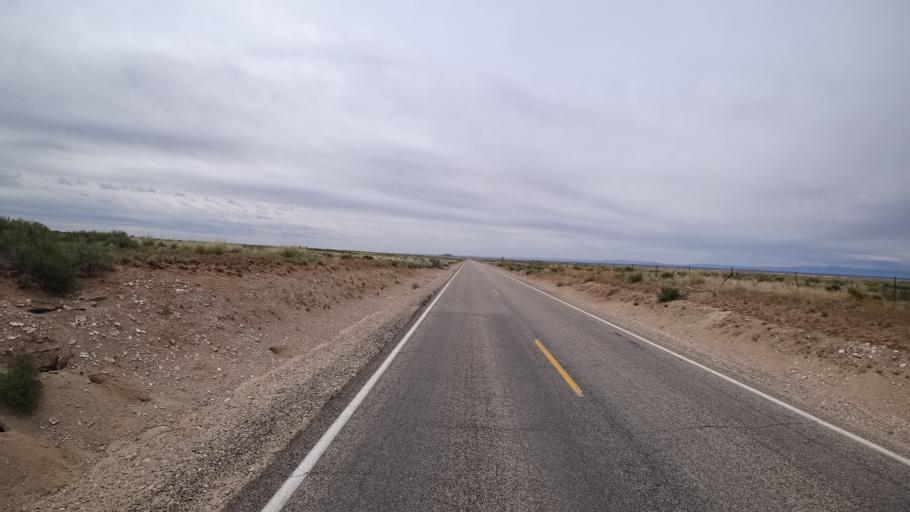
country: US
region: Idaho
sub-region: Ada County
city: Boise
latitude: 43.3634
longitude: -116.0049
